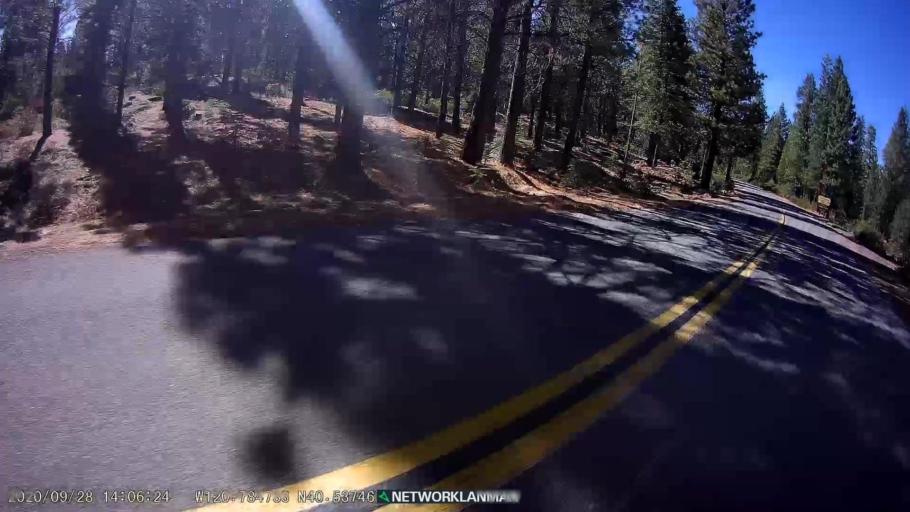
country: US
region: California
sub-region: Lassen County
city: Susanville
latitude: 40.5377
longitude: -120.7851
